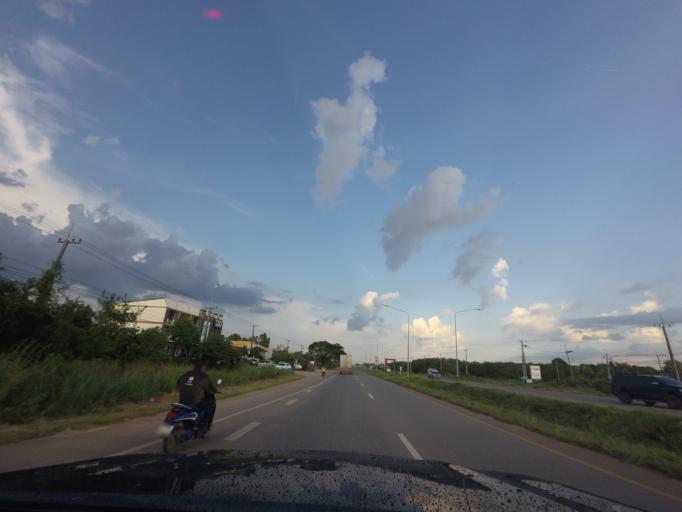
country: TH
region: Khon Kaen
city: Khon Kaen
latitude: 16.3879
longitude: 102.8340
